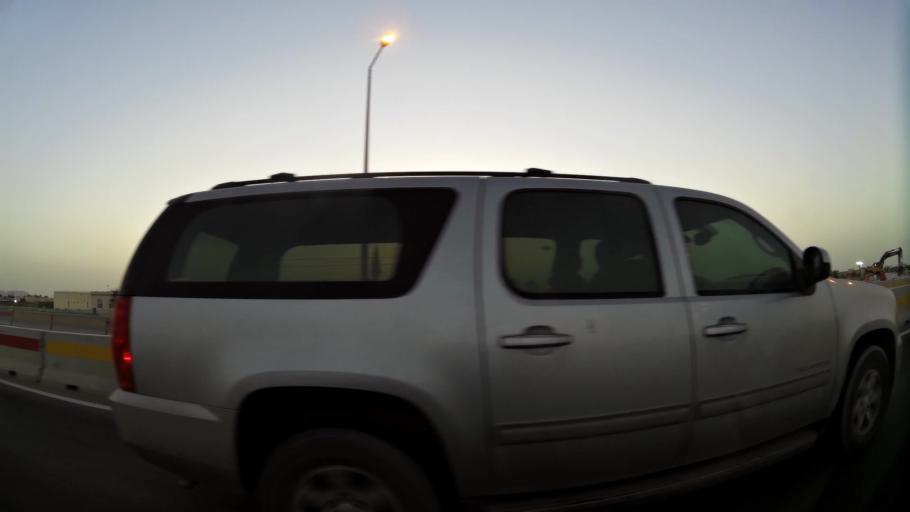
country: QA
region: Baladiyat ar Rayyan
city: Ar Rayyan
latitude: 25.3019
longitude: 51.4650
